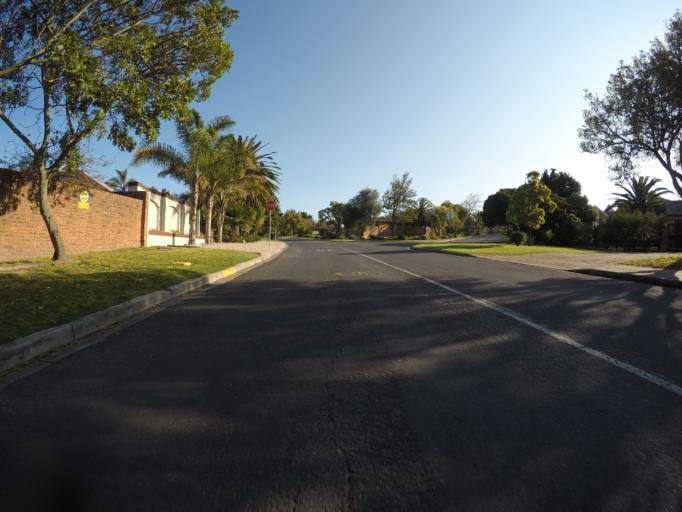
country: ZA
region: Western Cape
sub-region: City of Cape Town
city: Kraaifontein
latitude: -33.8492
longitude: 18.6583
